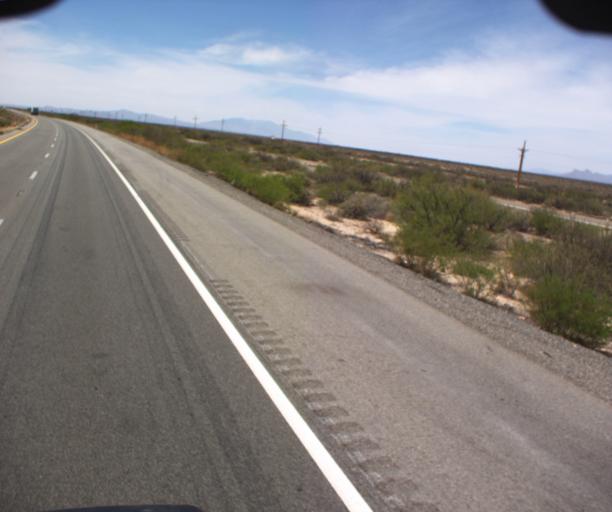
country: US
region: New Mexico
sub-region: Hidalgo County
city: Lordsburg
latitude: 32.2749
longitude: -109.2562
